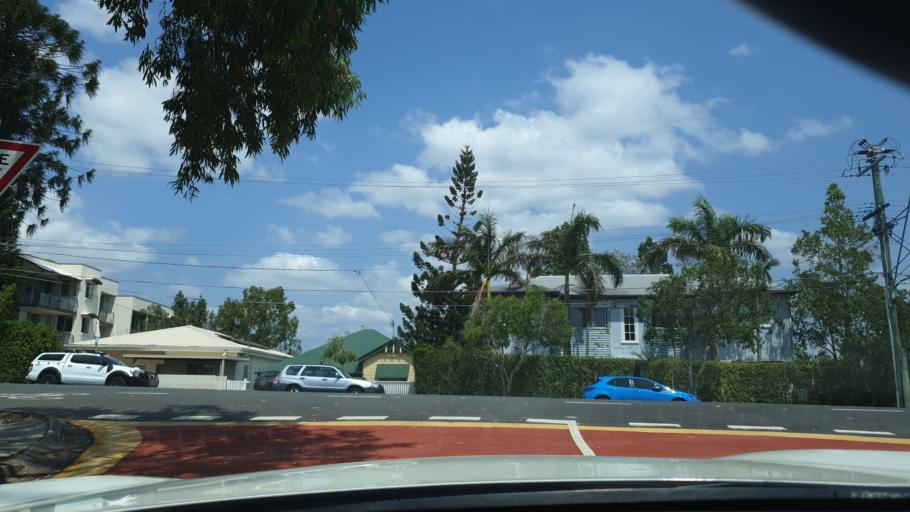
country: AU
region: Queensland
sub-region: Brisbane
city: South Brisbane
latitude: -27.4849
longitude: 153.0165
